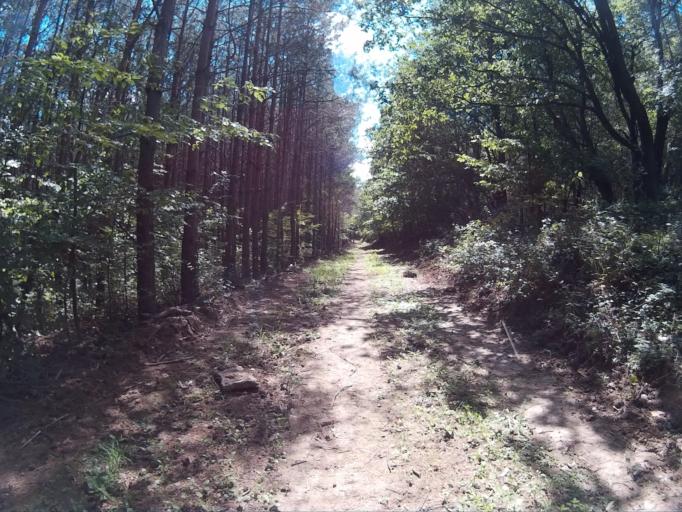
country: HU
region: Zala
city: Zalalovo
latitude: 46.8164
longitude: 16.6025
